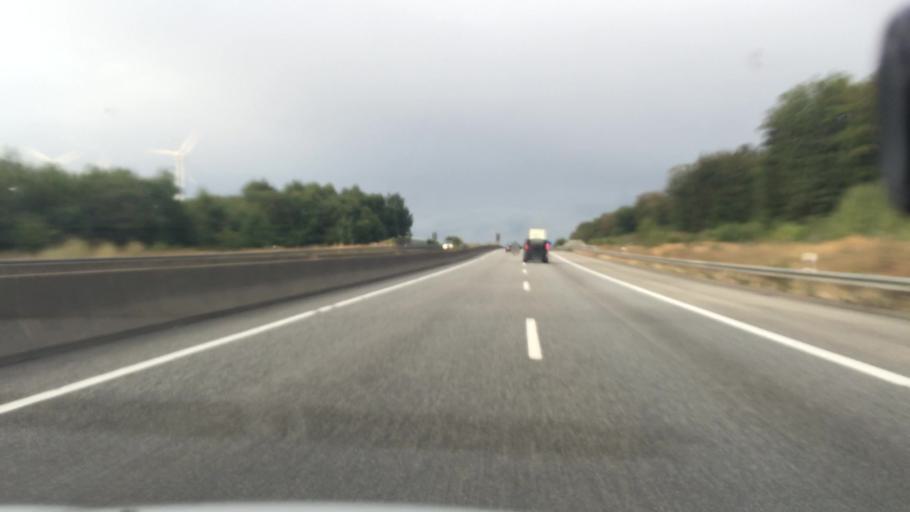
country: DE
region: Hesse
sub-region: Regierungsbezirk Giessen
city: Grunberg
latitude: 50.6493
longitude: 9.0030
